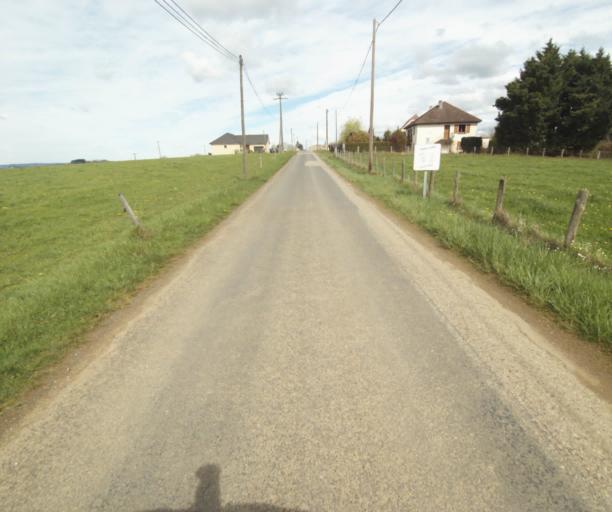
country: FR
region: Limousin
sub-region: Departement de la Correze
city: Laguenne
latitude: 45.2405
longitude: 1.8363
